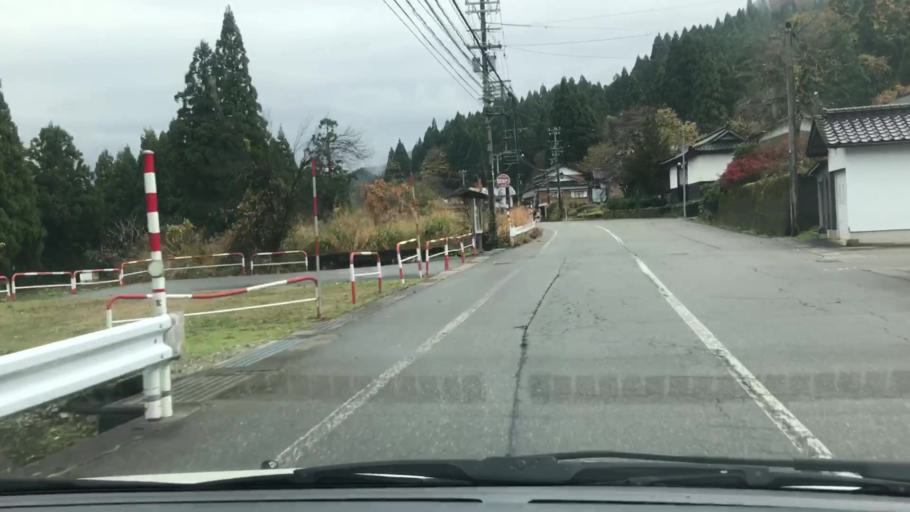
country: JP
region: Toyama
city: Kamiichi
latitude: 36.5701
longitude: 137.3520
